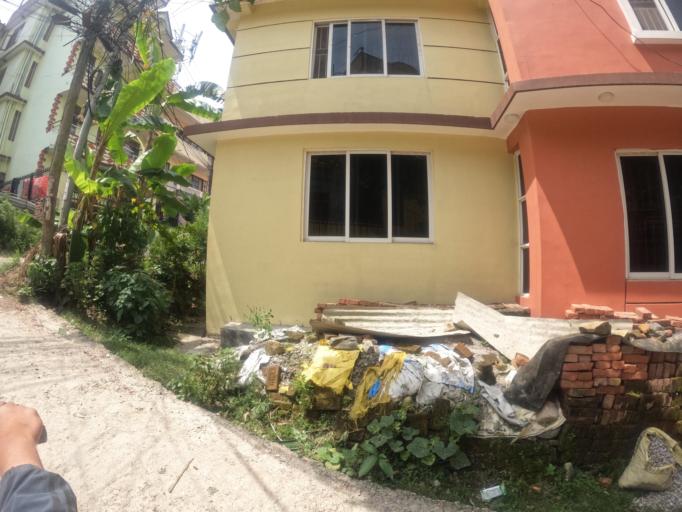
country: NP
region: Central Region
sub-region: Bagmati Zone
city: Kathmandu
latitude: 27.6787
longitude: 85.3692
